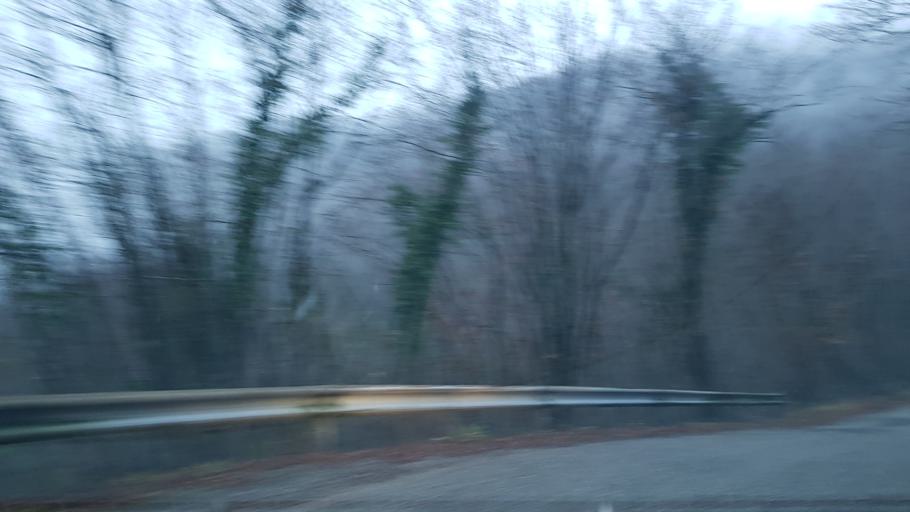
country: IT
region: Friuli Venezia Giulia
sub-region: Provincia di Udine
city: San Leonardo
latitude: 46.0875
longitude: 13.5576
